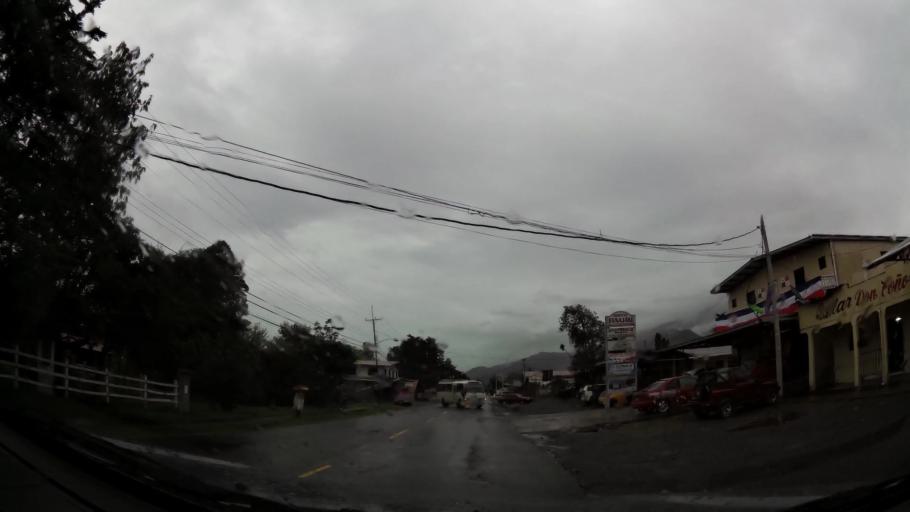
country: PA
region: Chiriqui
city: Volcan
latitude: 8.7876
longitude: -82.6521
